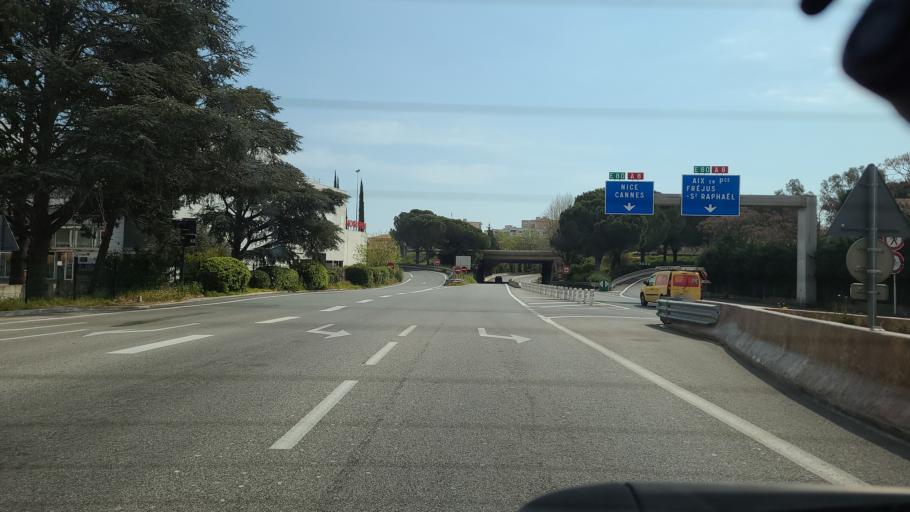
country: FR
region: Provence-Alpes-Cote d'Azur
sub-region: Departement des Alpes-Maritimes
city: Mandelieu-la-Napoule
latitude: 43.5449
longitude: 6.9382
